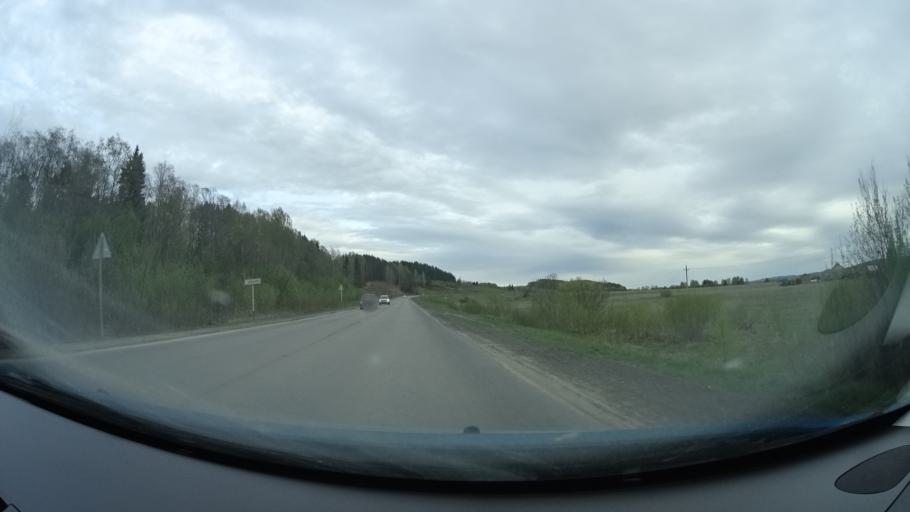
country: RU
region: Perm
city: Osa
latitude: 57.2215
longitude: 55.5895
